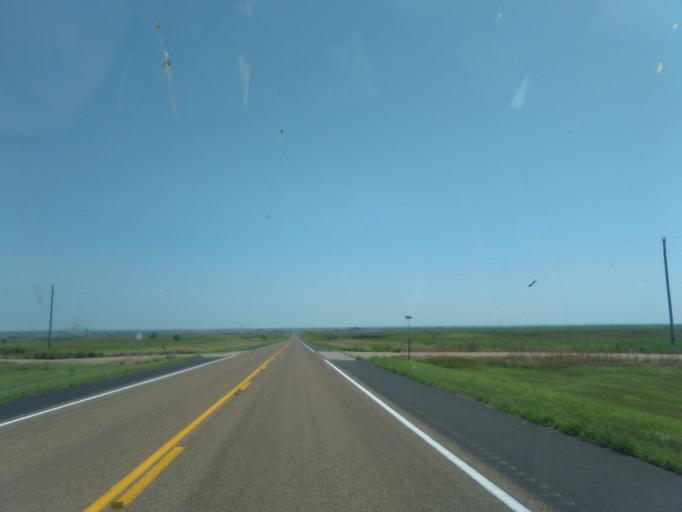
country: US
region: Nebraska
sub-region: Hitchcock County
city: Trenton
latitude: 40.2244
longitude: -100.9292
